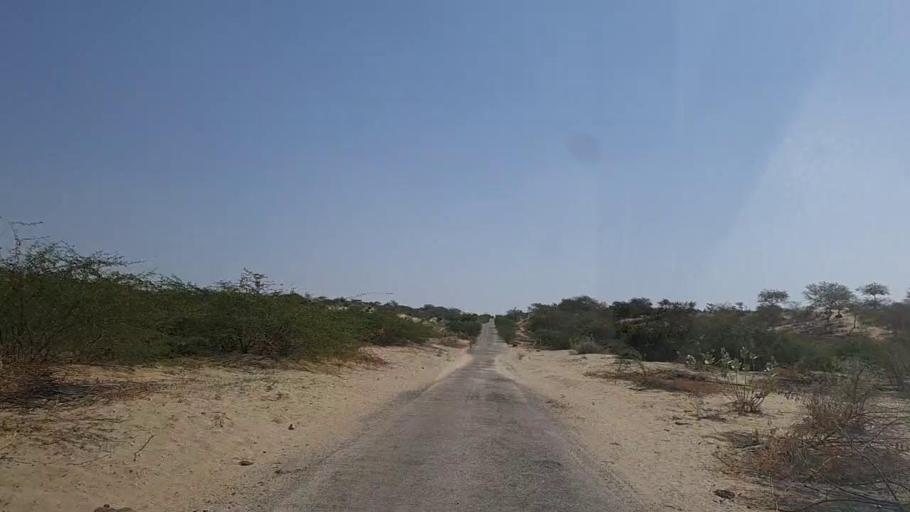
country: PK
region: Sindh
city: Diplo
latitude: 24.4885
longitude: 69.4427
